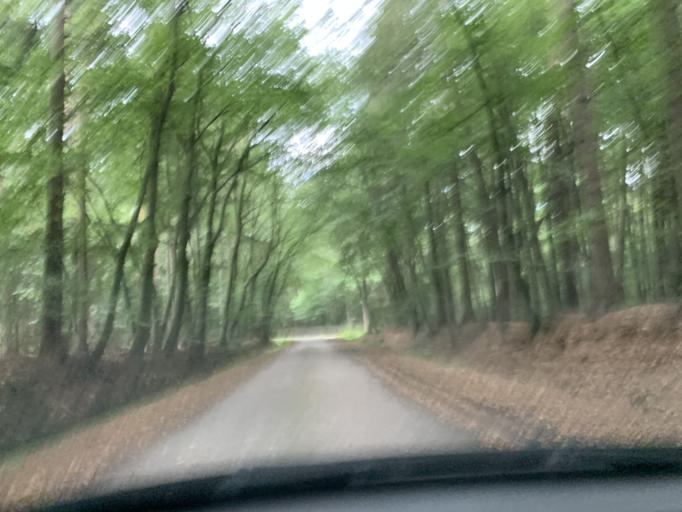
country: DE
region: Lower Saxony
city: Westerstede
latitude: 53.2687
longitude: 7.9944
